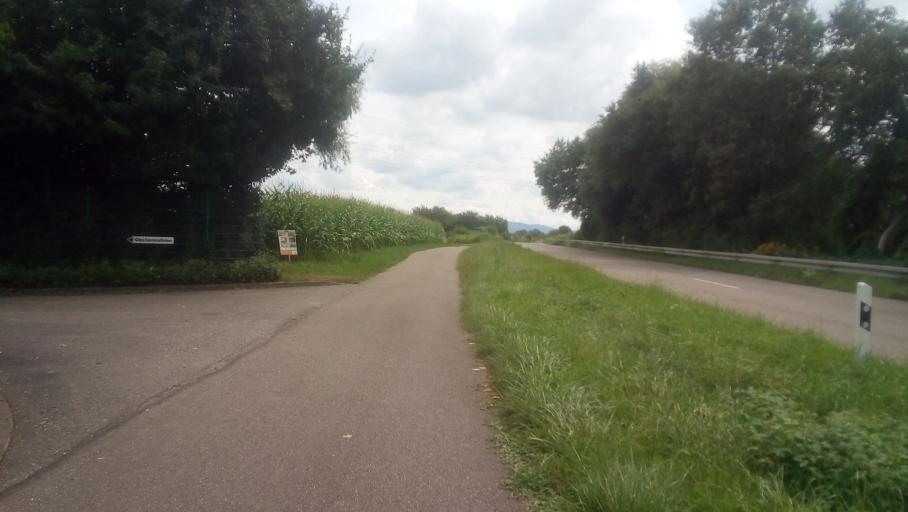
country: DE
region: Baden-Wuerttemberg
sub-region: Karlsruhe Region
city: Lichtenau
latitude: 48.7022
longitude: 7.9755
